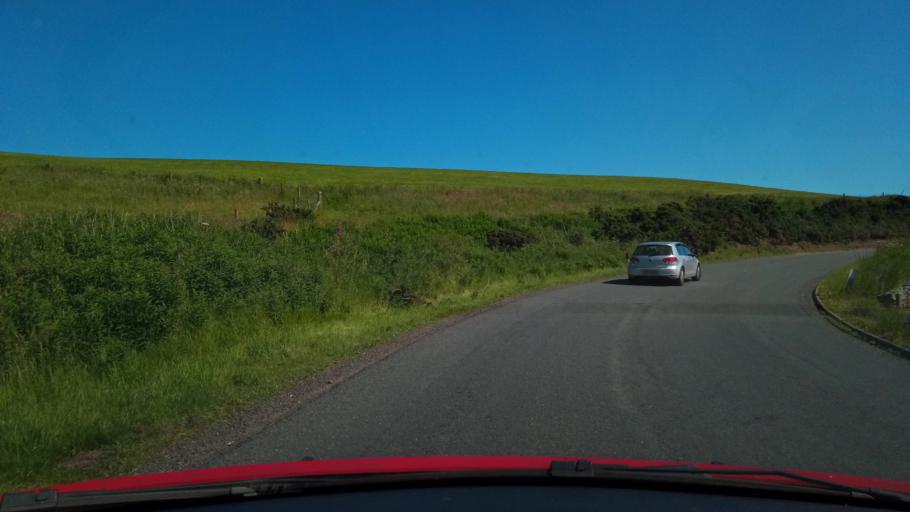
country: GB
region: Scotland
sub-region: The Scottish Borders
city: Duns
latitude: 55.8349
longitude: -2.3324
